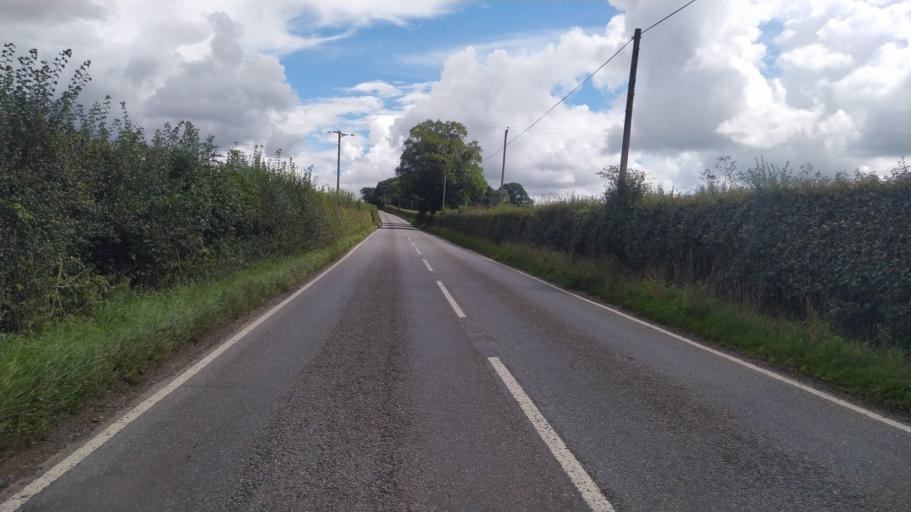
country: GB
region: England
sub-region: Dorset
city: Stalbridge
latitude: 50.9093
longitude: -2.4083
